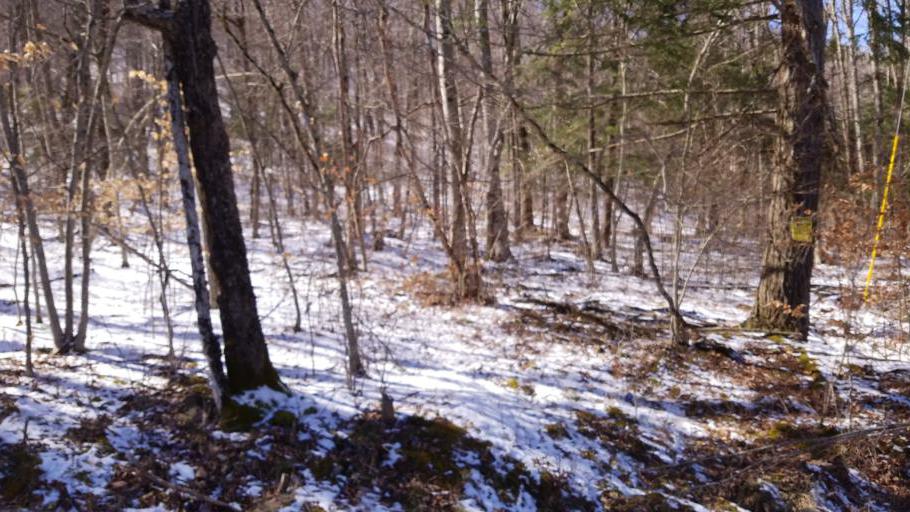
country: US
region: New York
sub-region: Allegany County
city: Wellsville
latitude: 42.0170
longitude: -77.9262
